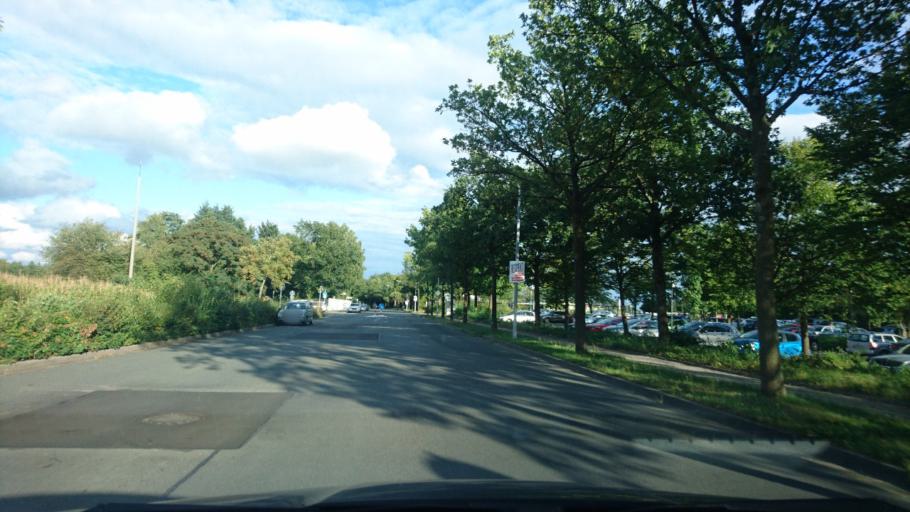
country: DE
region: Bavaria
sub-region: Upper Franconia
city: Heinersreuth
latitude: 49.9450
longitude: 11.5330
